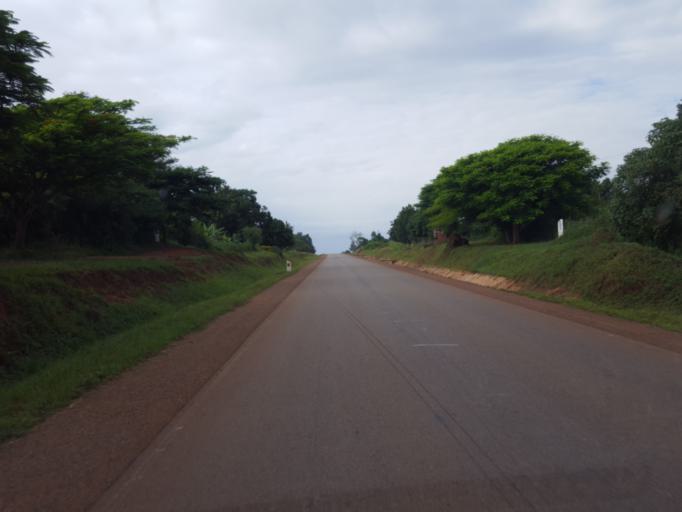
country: UG
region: Central Region
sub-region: Kyankwanzi District
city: Kyankwanzi
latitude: 1.1935
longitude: 31.5629
